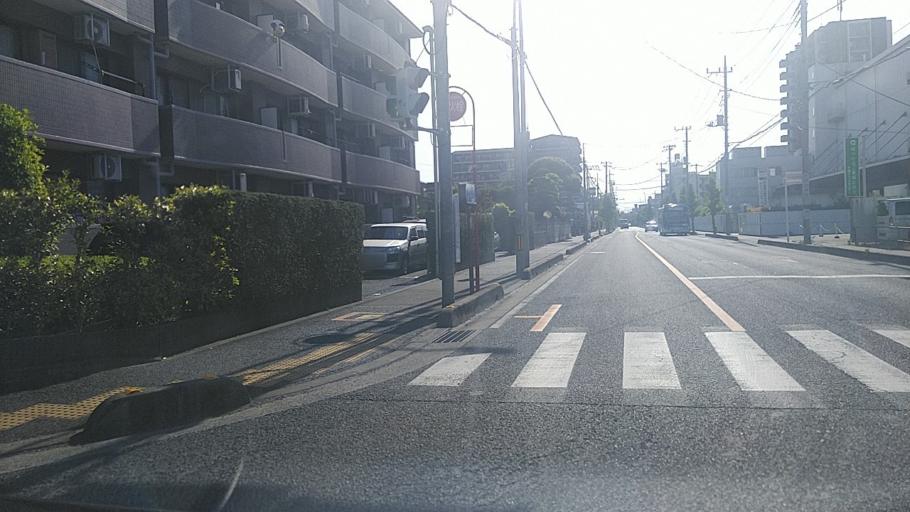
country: JP
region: Saitama
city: Shimotoda
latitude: 35.8078
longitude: 139.6691
